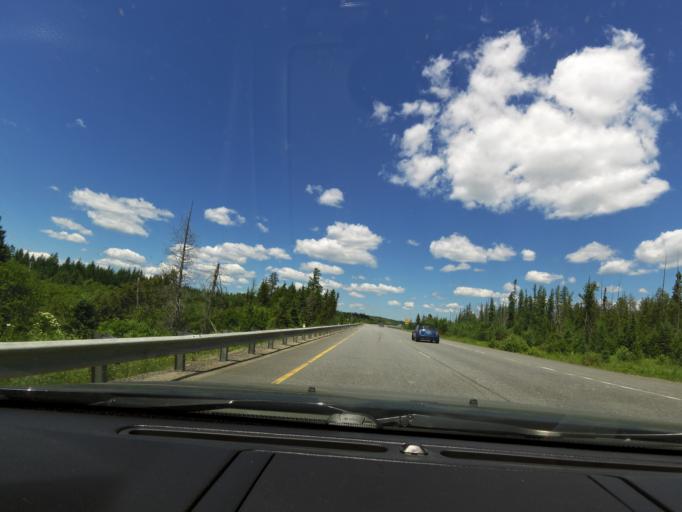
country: CA
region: Ontario
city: Huntsville
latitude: 45.4340
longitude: -79.2403
